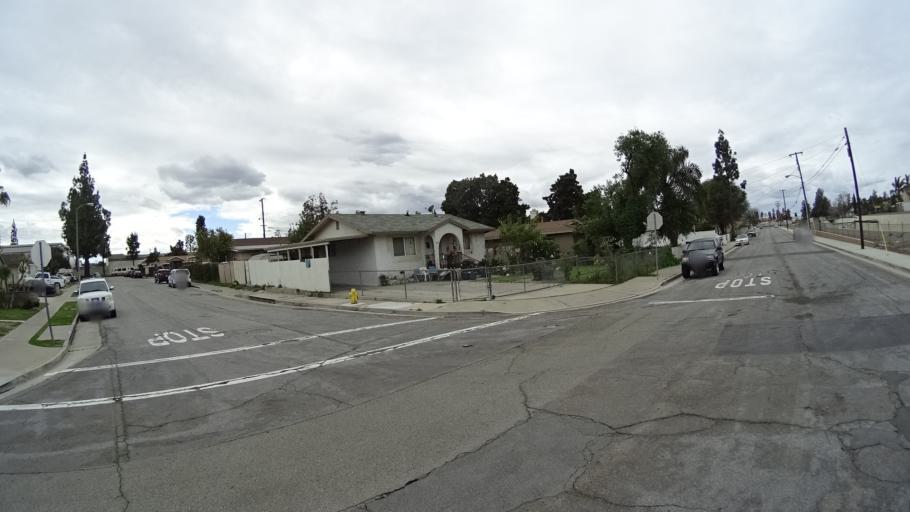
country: US
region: California
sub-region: Orange County
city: Yorba Linda
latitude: 33.8663
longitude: -117.8283
